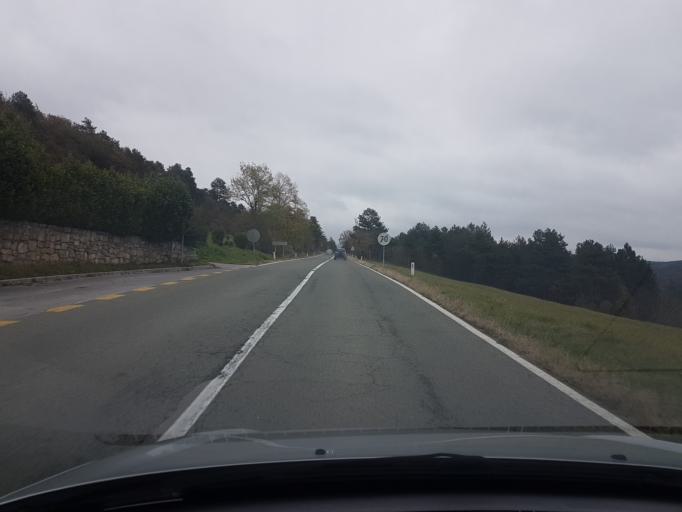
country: SI
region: Divaca
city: Divaca
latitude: 45.7317
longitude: 13.9591
